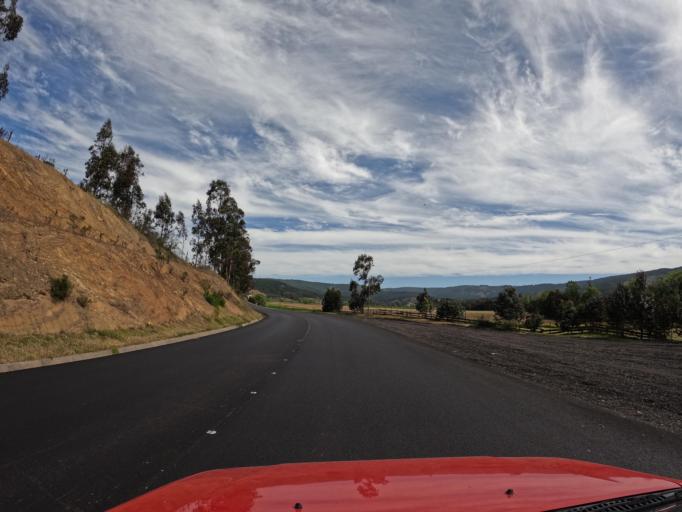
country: CL
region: Maule
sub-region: Provincia de Talca
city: Constitucion
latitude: -35.0729
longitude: -72.0398
